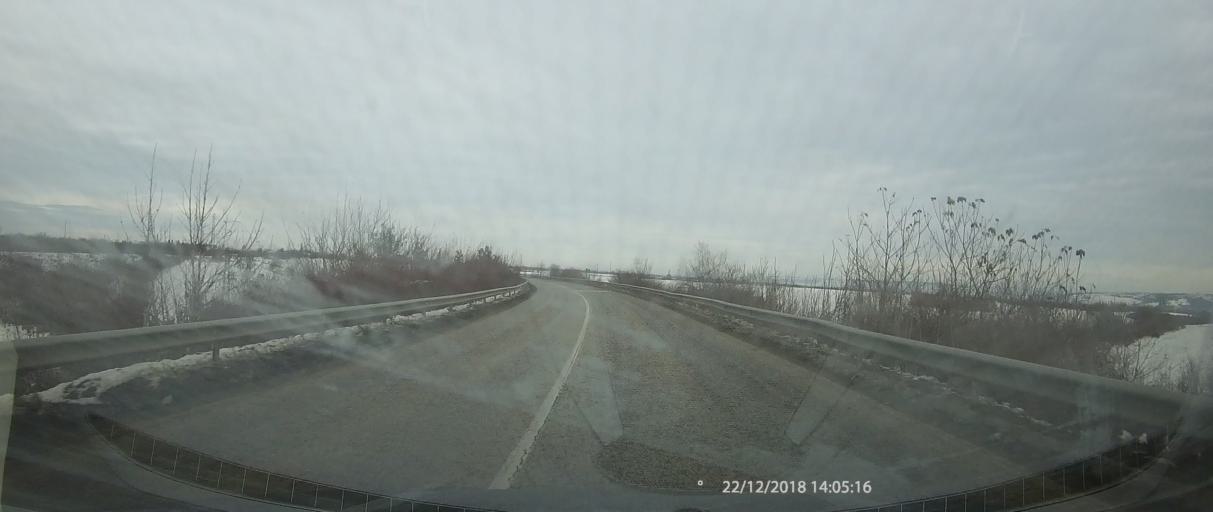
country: BG
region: Pleven
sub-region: Obshtina Dolni Dubnik
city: Dolni Dubnik
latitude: 43.4000
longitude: 24.4549
